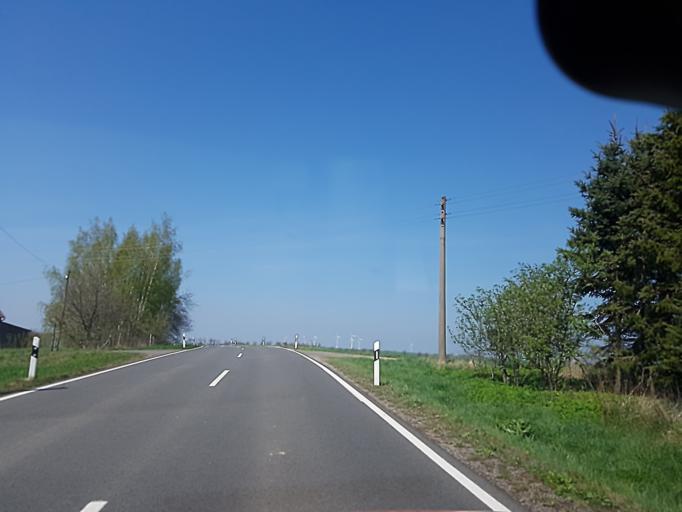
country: DE
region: Saxony
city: Ostrau
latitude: 51.2161
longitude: 12.8746
